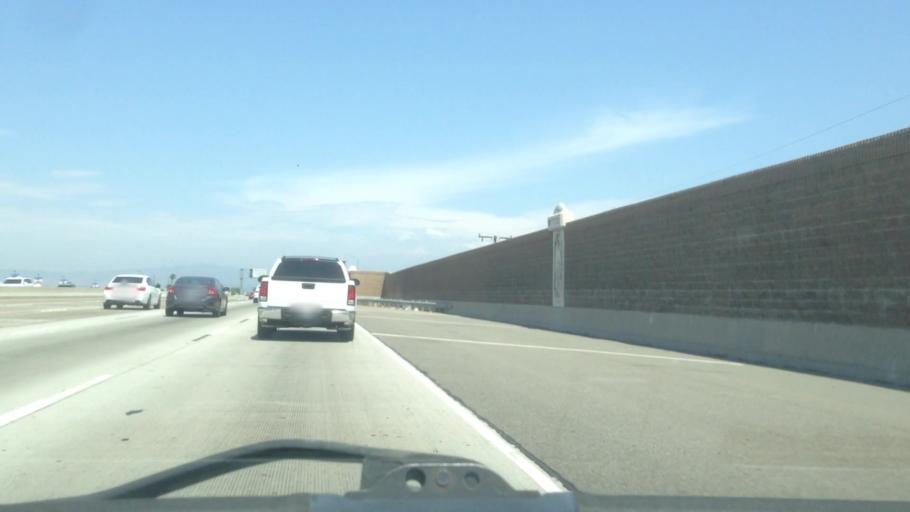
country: US
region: California
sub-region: Orange County
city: Garden Grove
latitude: 33.7624
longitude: -117.9322
